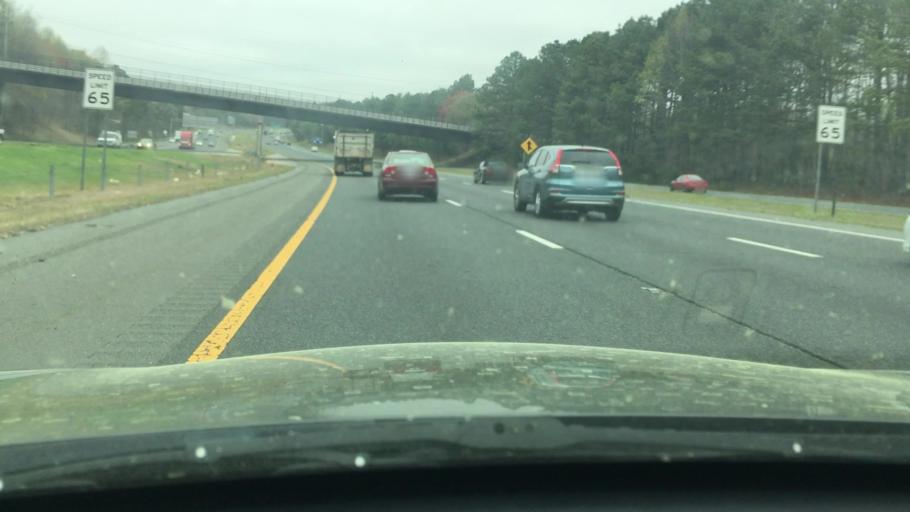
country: US
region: North Carolina
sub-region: Wake County
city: Cary
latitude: 35.7698
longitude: -78.7380
